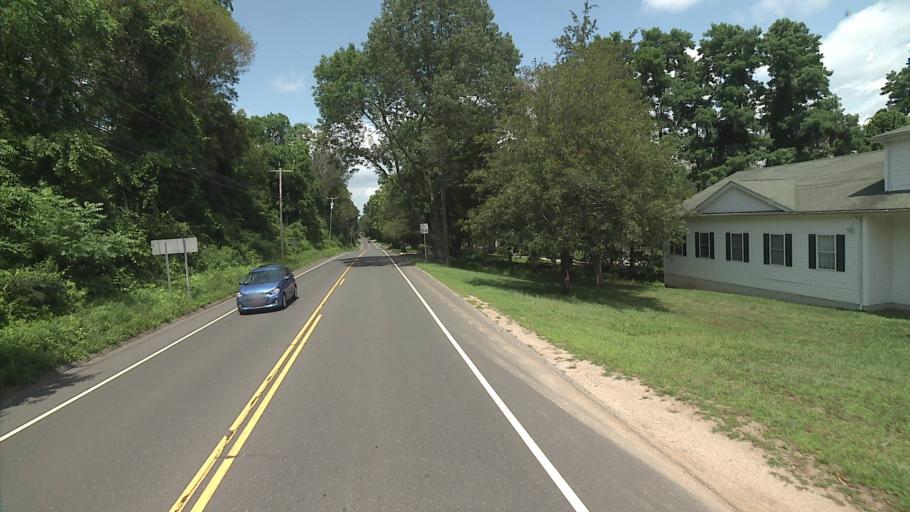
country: US
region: Connecticut
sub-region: Middlesex County
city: East Haddam
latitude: 41.4288
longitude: -72.4514
